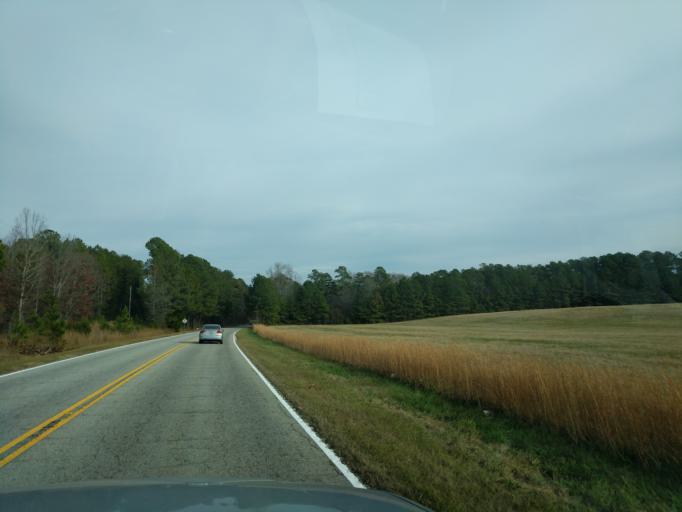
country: US
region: South Carolina
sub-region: Pickens County
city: Central
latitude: 34.7058
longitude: -82.7065
